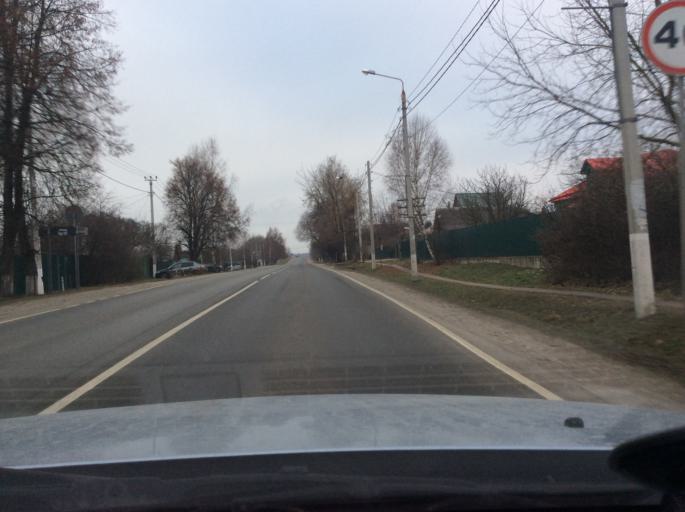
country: RU
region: Moskovskaya
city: Filimonki
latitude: 55.5219
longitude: 37.3749
